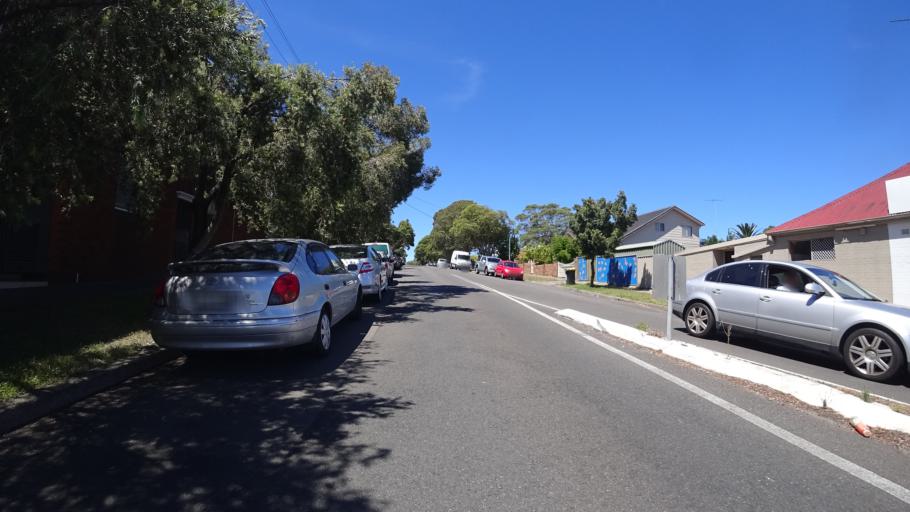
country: AU
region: New South Wales
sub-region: Rockdale
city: Bexley
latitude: -33.9557
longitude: 151.1257
